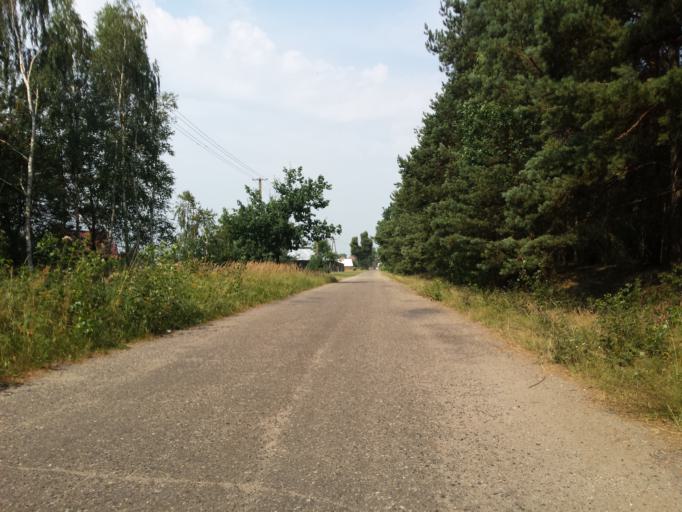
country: PL
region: Greater Poland Voivodeship
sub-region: Powiat czarnkowsko-trzcianecki
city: Polajewo
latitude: 52.7702
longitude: 16.6540
